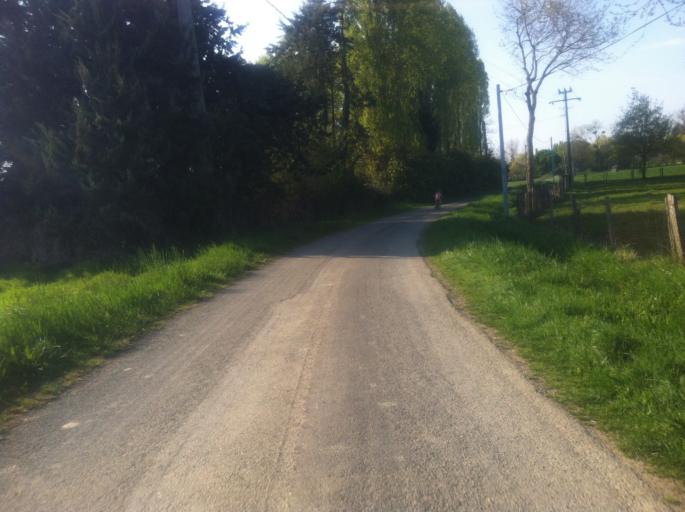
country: FR
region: Brittany
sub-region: Departement d'Ille-et-Vilaine
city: Bruz
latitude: 48.0133
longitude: -1.7266
